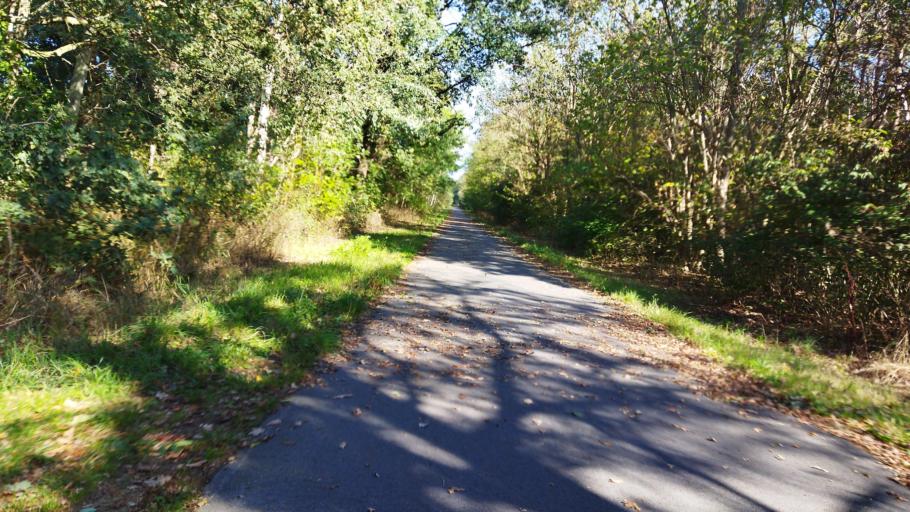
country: DE
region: Lower Saxony
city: Ohne
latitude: 52.2662
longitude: 7.3139
